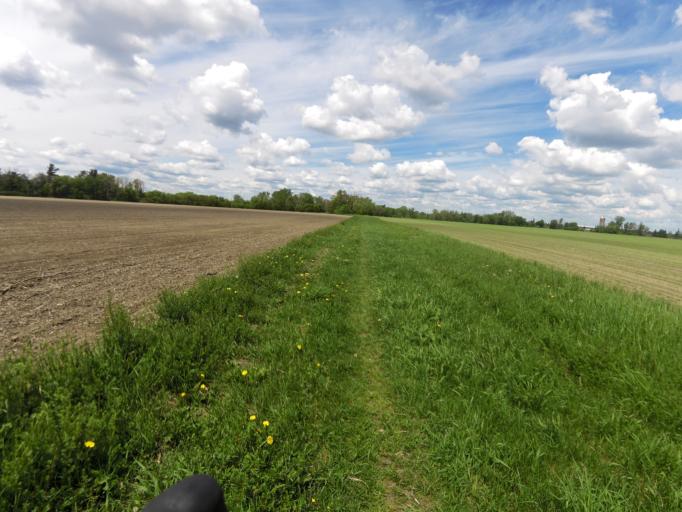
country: CA
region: Ontario
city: Ottawa
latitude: 45.4150
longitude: -75.5903
